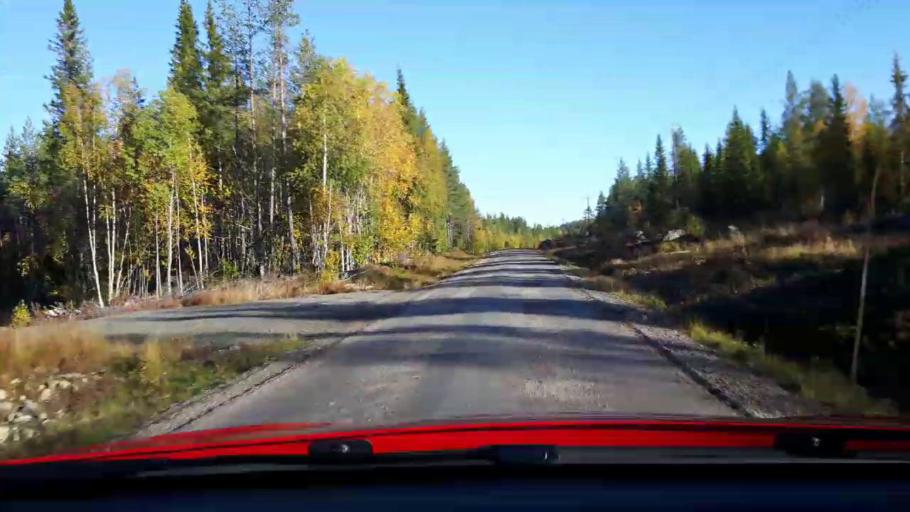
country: SE
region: Jaemtland
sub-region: Stroemsunds Kommun
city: Stroemsund
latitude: 64.3890
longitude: 15.1508
